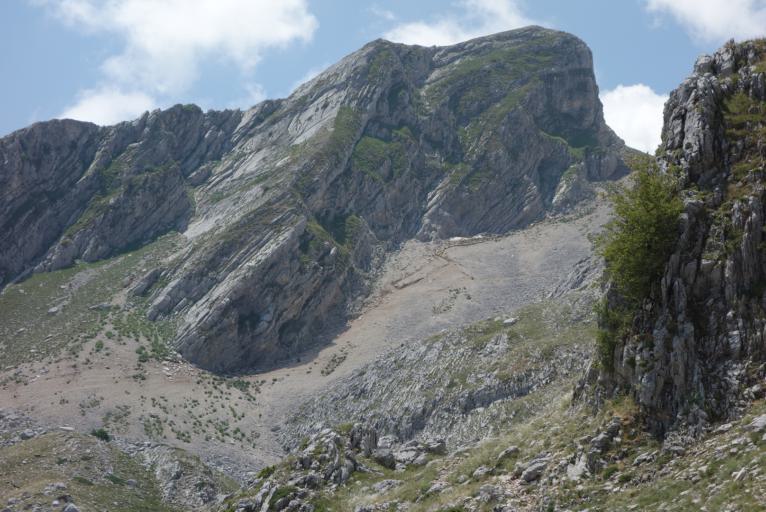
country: AL
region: Gjirokaster
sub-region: Rrethi i Gjirokastres
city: Saraqinishte
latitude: 40.1442
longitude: 20.2591
